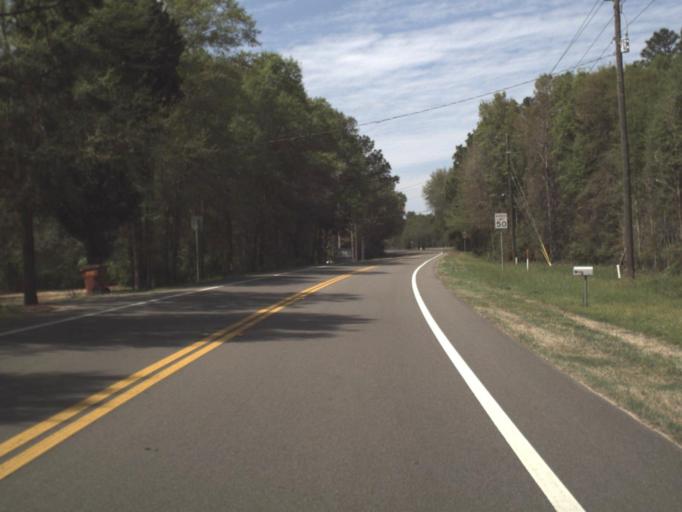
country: US
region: Florida
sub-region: Okaloosa County
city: Crestview
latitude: 30.7122
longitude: -86.7550
